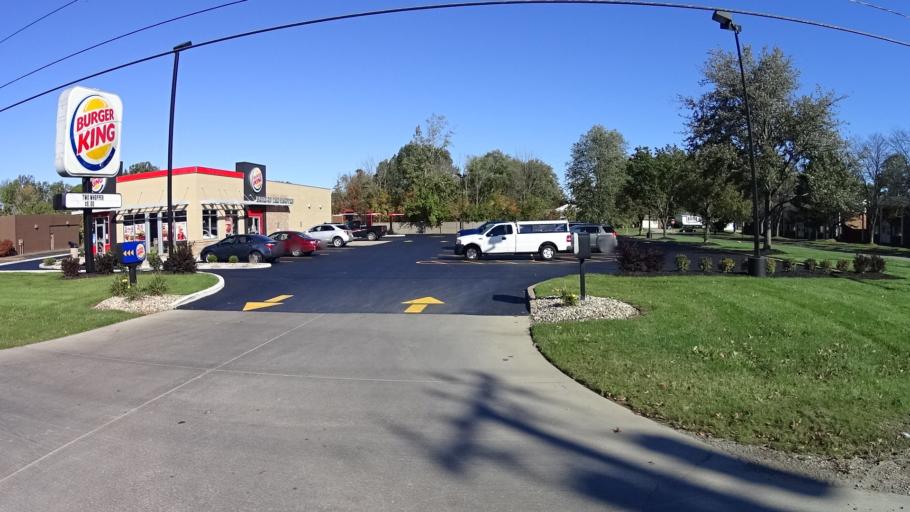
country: US
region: Ohio
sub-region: Lorain County
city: Amherst
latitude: 41.4183
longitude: -82.2005
